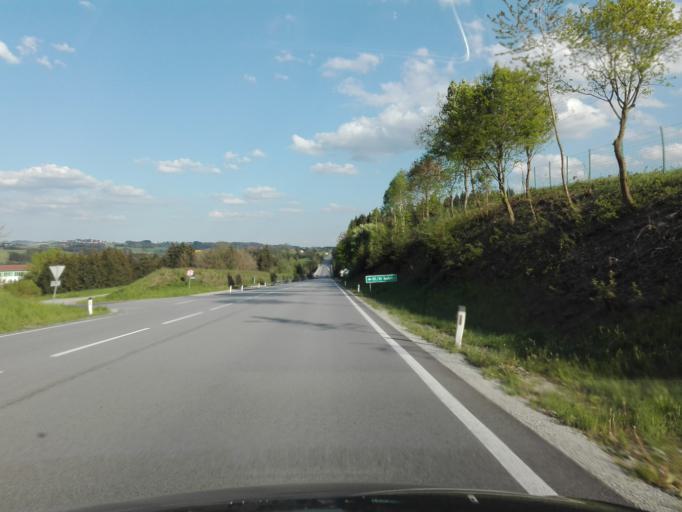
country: AT
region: Upper Austria
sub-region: Politischer Bezirk Rohrbach
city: Kleinzell im Muehlkreis
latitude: 48.4799
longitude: 13.9892
